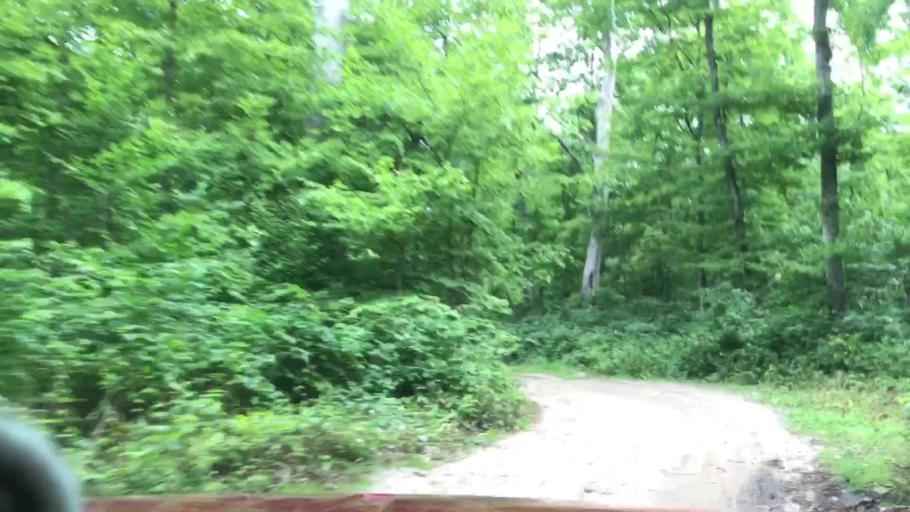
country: US
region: Michigan
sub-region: Charlevoix County
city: Charlevoix
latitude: 45.7226
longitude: -85.5646
